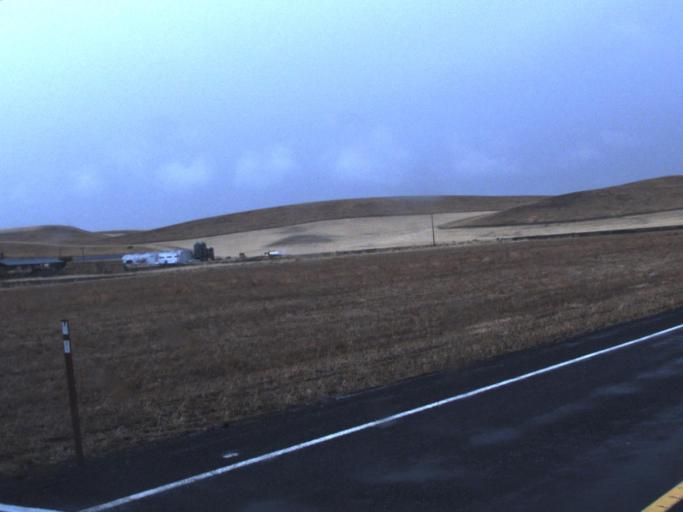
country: US
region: Washington
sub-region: Spokane County
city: Cheney
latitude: 47.1826
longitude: -117.8711
